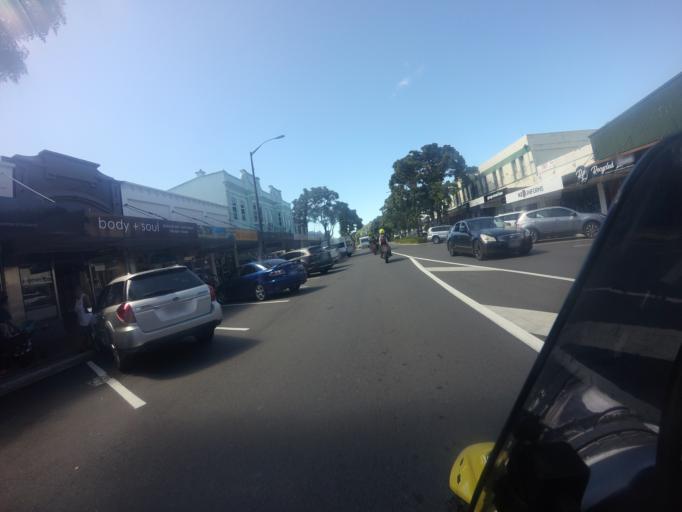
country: NZ
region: Bay of Plenty
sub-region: Whakatane District
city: Whakatane
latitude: -37.9507
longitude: 176.9975
